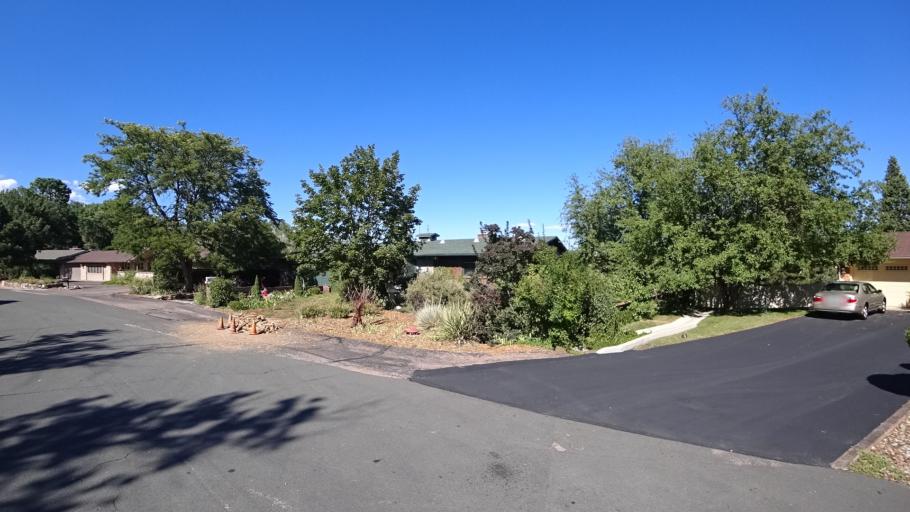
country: US
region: Colorado
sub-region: El Paso County
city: Colorado Springs
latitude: 38.8610
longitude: -104.8566
